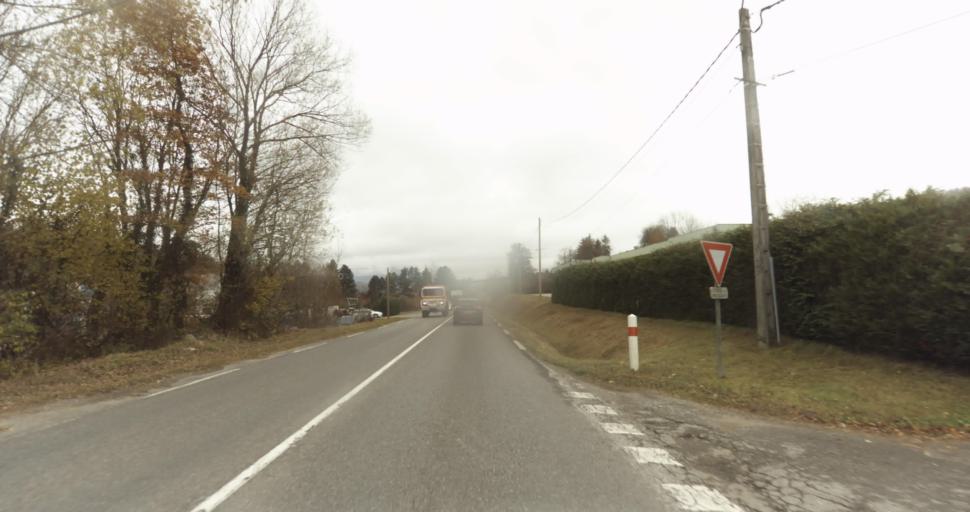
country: FR
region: Rhone-Alpes
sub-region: Departement de la Haute-Savoie
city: Saint-Martin-Bellevue
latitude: 45.9714
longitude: 6.1639
